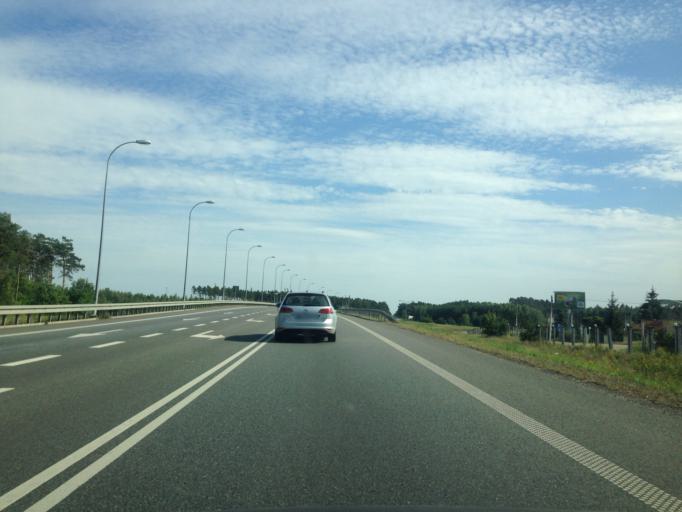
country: PL
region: Kujawsko-Pomorskie
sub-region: Powiat torunski
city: Lubicz Dolny
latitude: 52.9709
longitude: 18.6800
